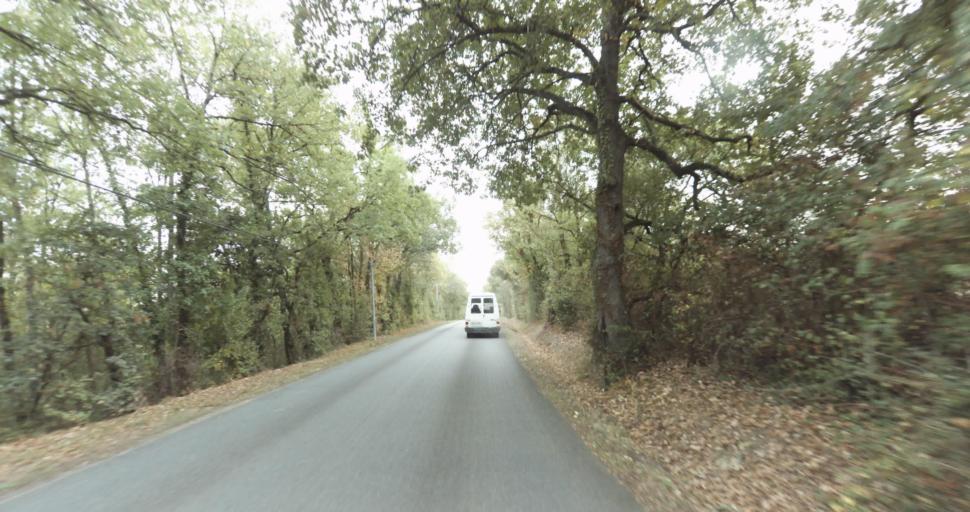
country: FR
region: Midi-Pyrenees
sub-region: Departement du Gers
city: Auch
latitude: 43.6770
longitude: 0.5961
